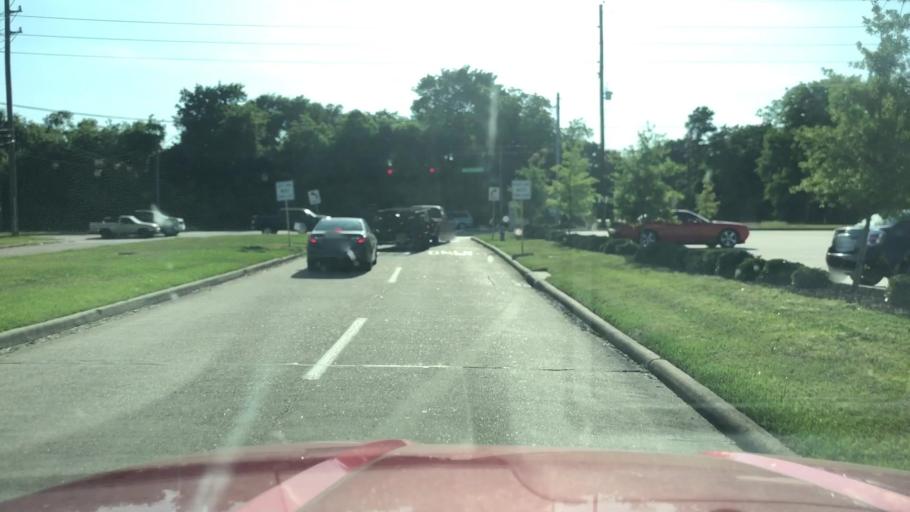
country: US
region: Texas
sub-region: Harris County
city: Hudson
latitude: 29.9465
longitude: -95.4974
